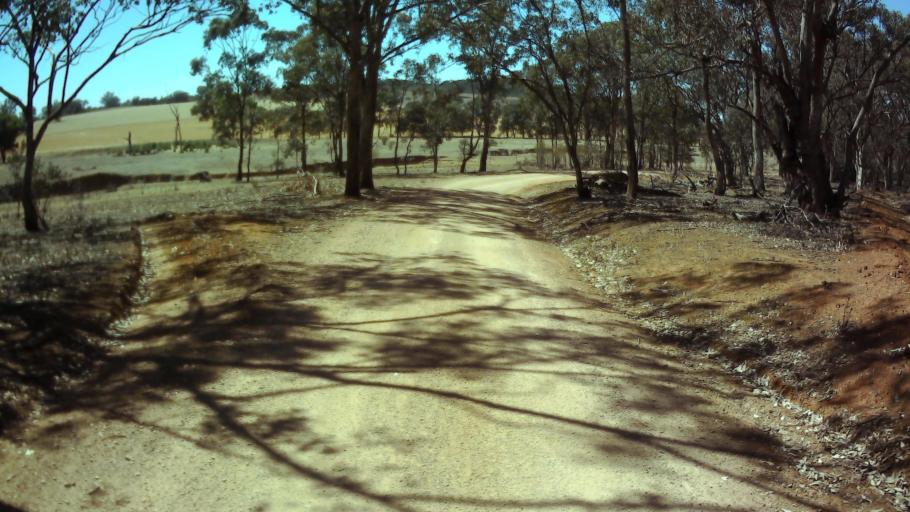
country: AU
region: New South Wales
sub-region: Weddin
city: Grenfell
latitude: -33.9480
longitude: 148.0836
